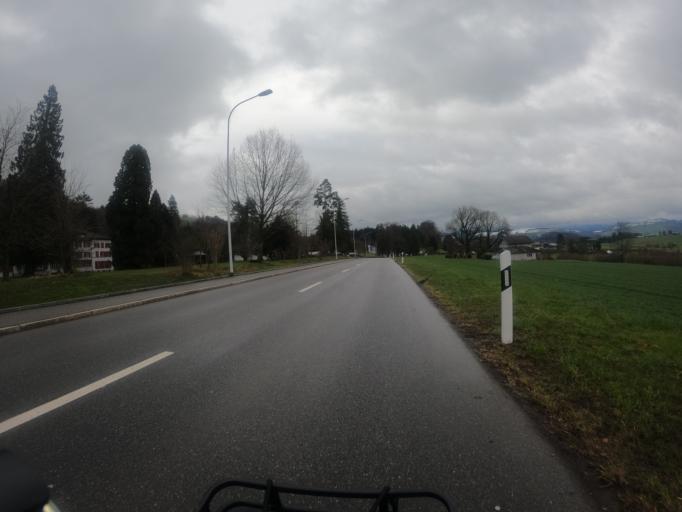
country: CH
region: Zurich
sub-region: Bezirk Affoltern
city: Hausen am Albis / Hausen (Dorf)
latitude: 47.2382
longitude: 8.5406
